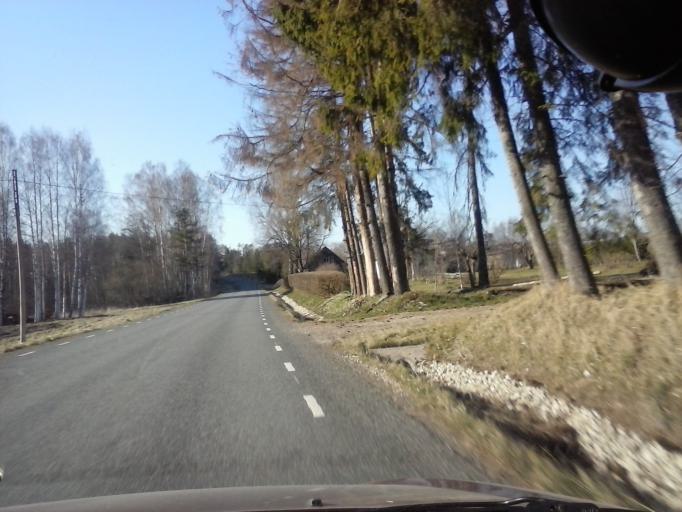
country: EE
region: Tartu
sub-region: UElenurme vald
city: Ulenurme
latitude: 58.1732
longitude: 26.8335
